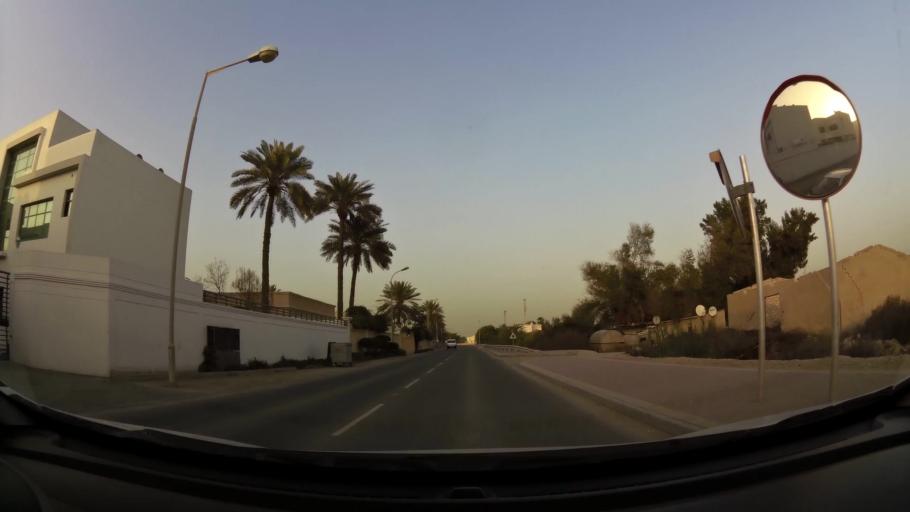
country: BH
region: Northern
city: Madinat `Isa
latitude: 26.1946
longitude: 50.4690
